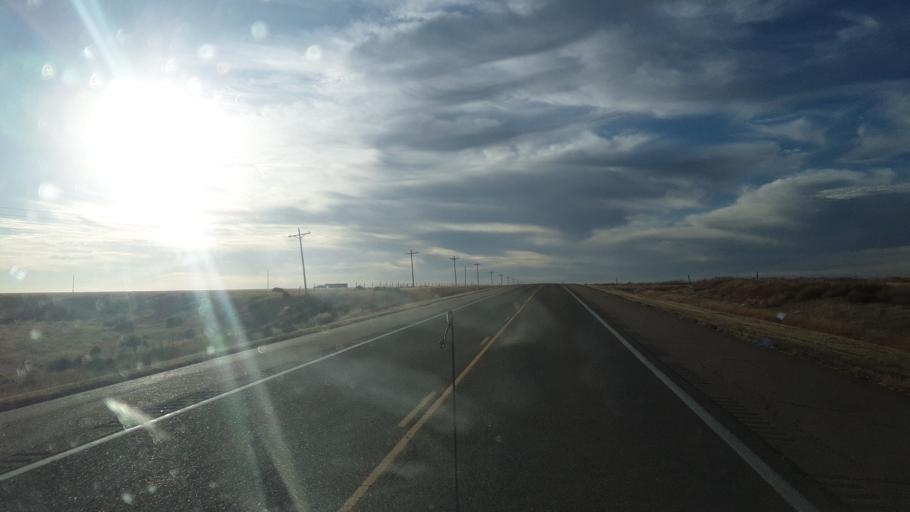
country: US
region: Kansas
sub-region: Kearny County
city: Lakin
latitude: 37.9440
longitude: -101.4541
